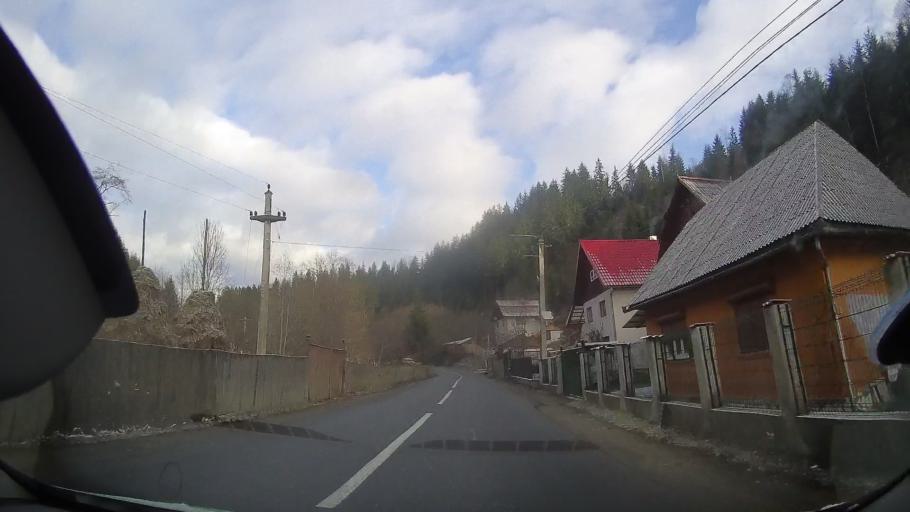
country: RO
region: Alba
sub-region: Comuna Albac
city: Albac
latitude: 46.4583
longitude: 22.9755
